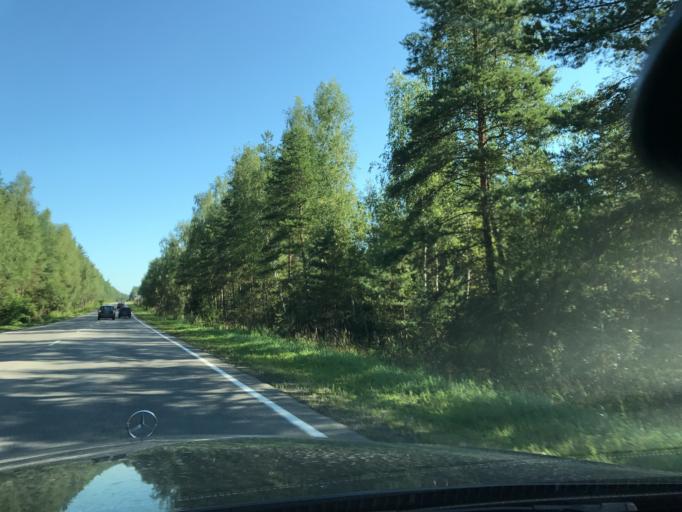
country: RU
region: Moskovskaya
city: Noginsk-9
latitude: 56.0857
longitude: 38.5778
